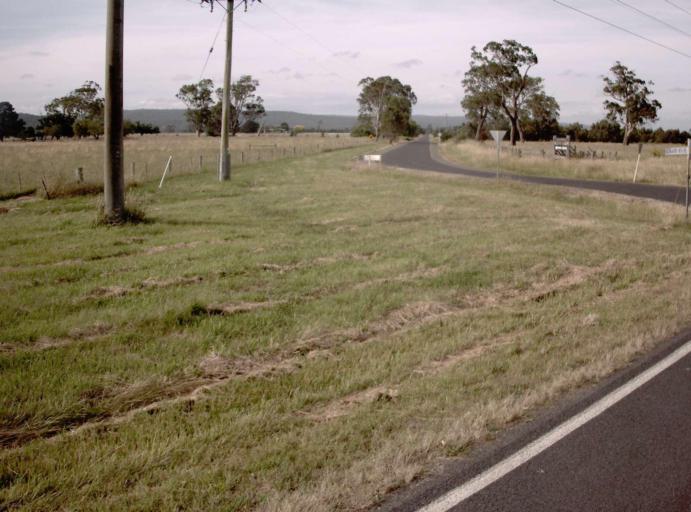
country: AU
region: Victoria
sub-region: Latrobe
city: Traralgon
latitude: -38.1191
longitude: 146.5758
